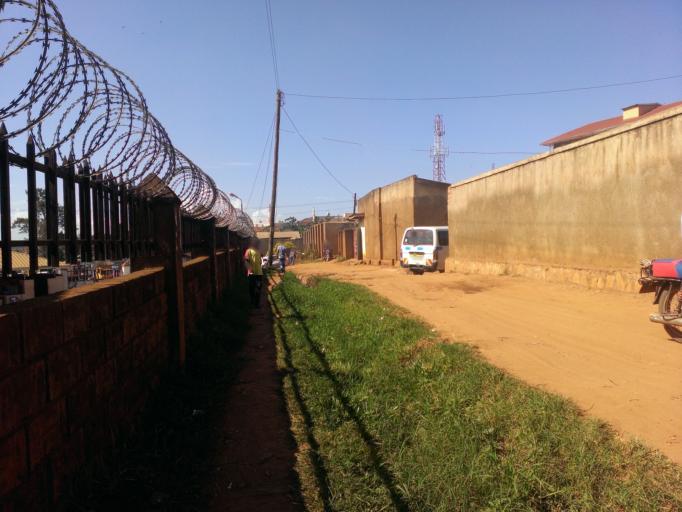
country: UG
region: Central Region
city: Kampala Central Division
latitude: 0.3240
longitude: 32.5645
